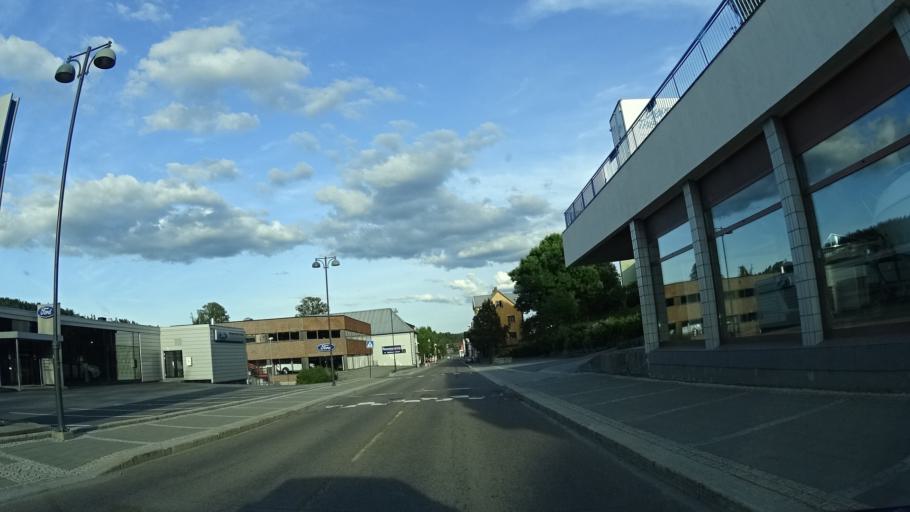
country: NO
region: Ostfold
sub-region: Eidsberg
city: Mysen
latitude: 59.5553
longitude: 11.3271
